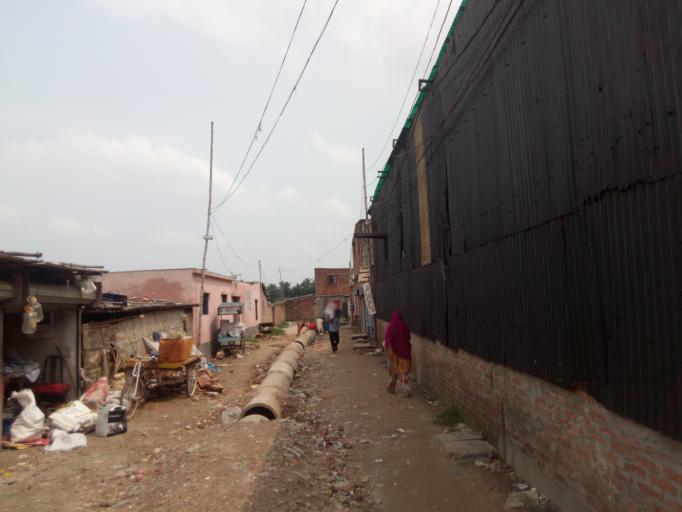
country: BD
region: Dhaka
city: Azimpur
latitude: 23.7432
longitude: 90.3573
